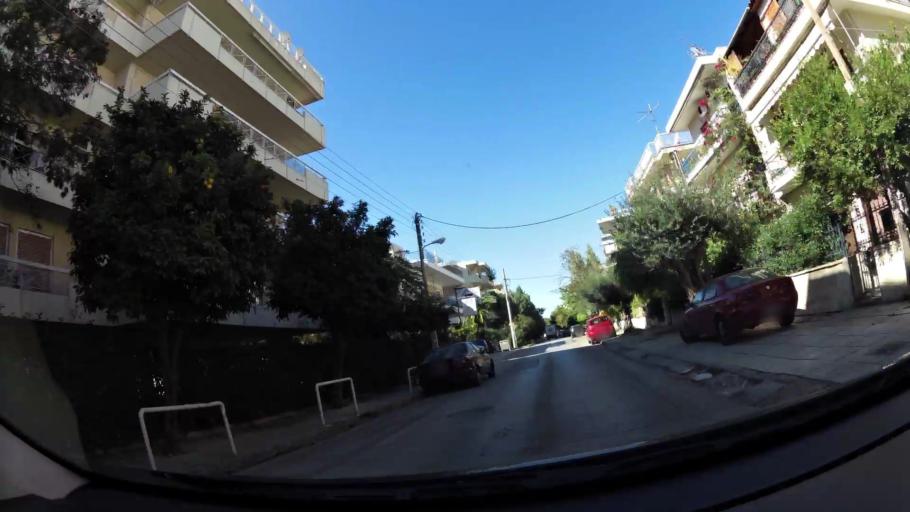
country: GR
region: Attica
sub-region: Nomarchia Athinas
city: Khalandrion
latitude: 38.0281
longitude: 23.8071
